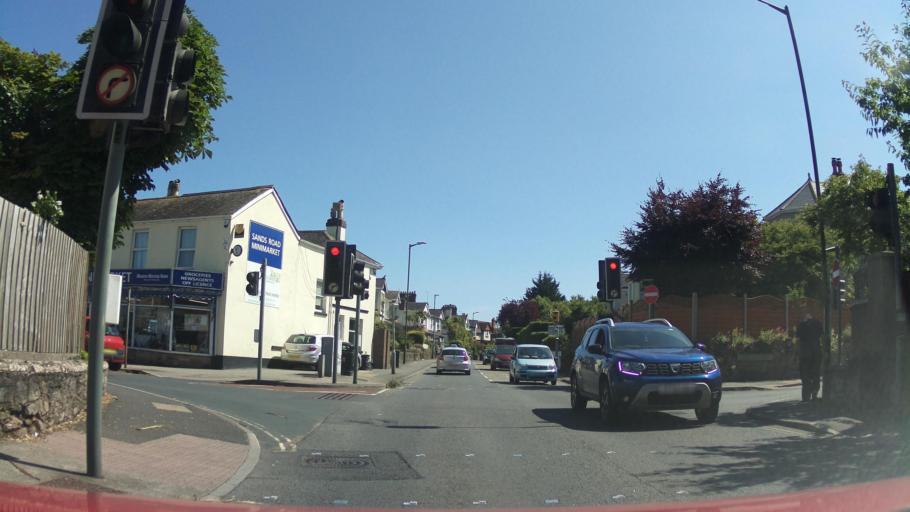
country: GB
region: England
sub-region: Borough of Torbay
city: Paignton
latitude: 50.4323
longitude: -3.5661
